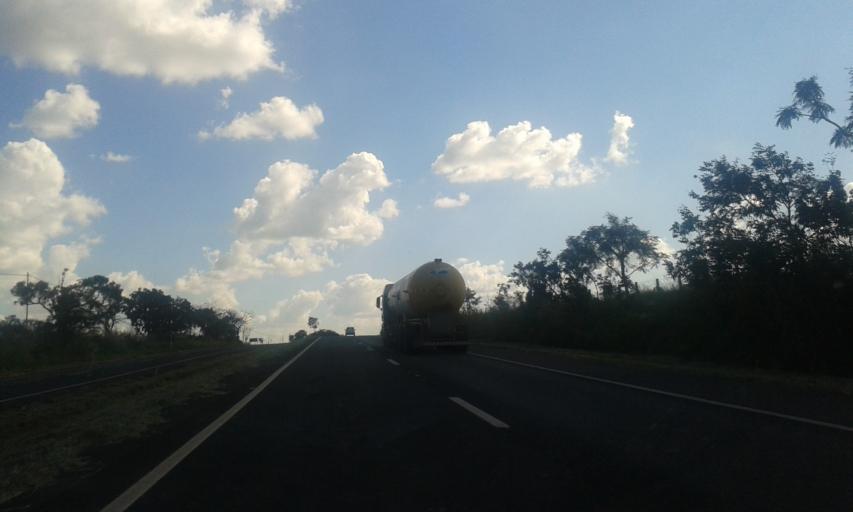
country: BR
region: Minas Gerais
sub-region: Monte Alegre De Minas
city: Monte Alegre de Minas
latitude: -18.8916
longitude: -48.6791
